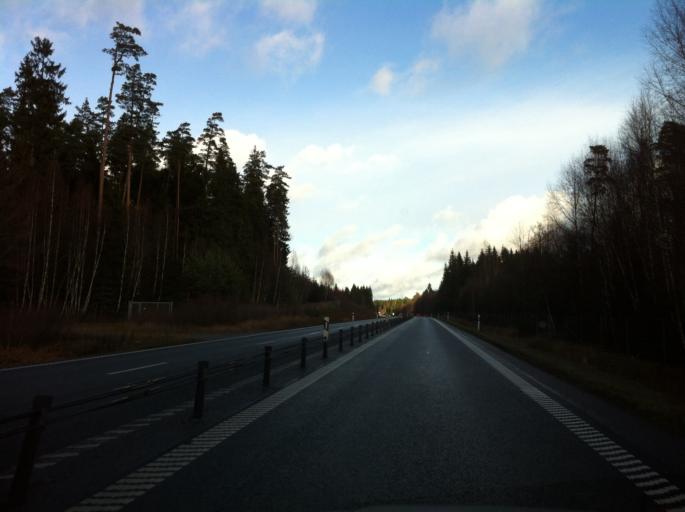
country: SE
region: Skane
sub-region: Osby Kommun
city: Osby
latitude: 56.4088
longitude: 14.0444
